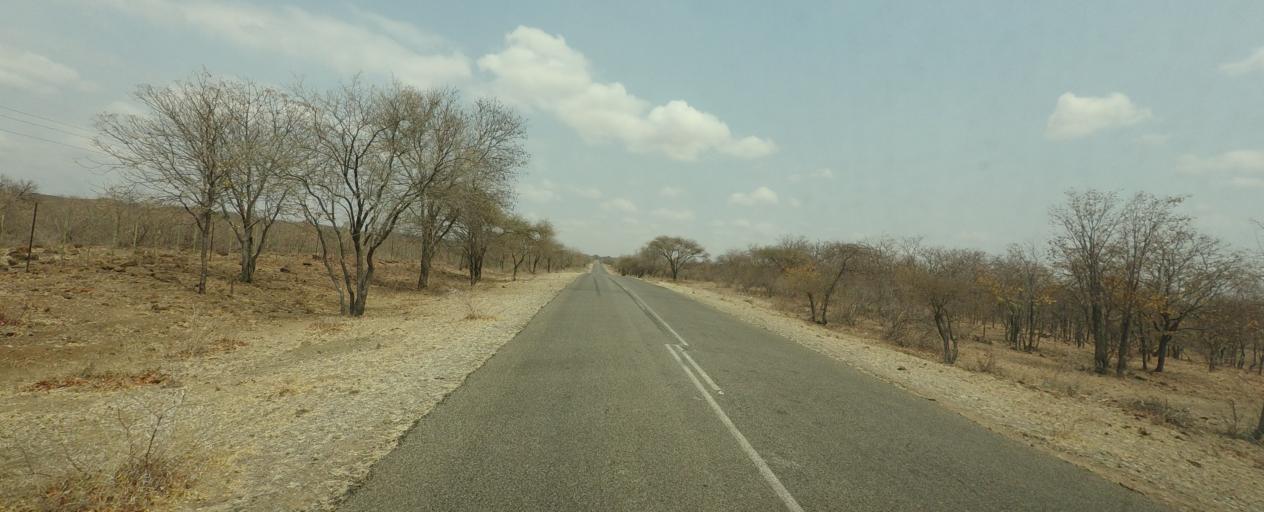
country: ZA
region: Limpopo
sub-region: Vhembe District Municipality
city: Mutale
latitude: -22.4204
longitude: 30.9578
